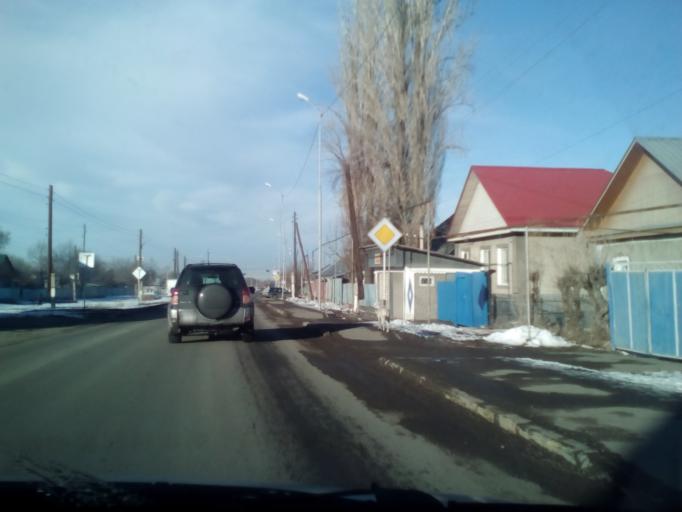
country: KZ
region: Almaty Oblysy
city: Burunday
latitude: 43.1771
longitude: 76.4144
